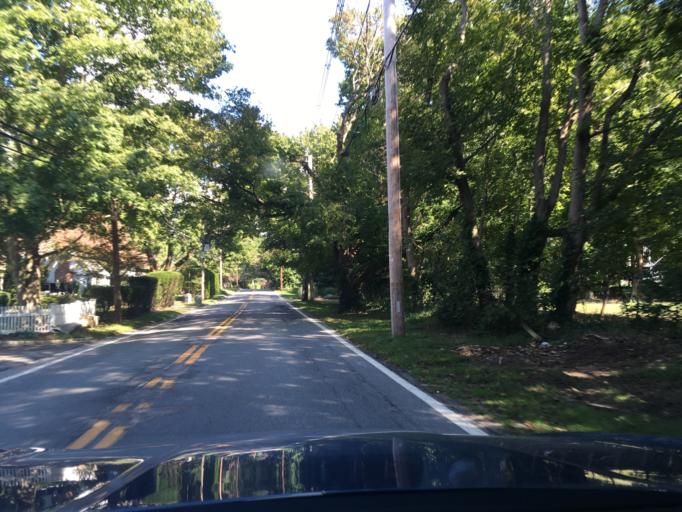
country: US
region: Rhode Island
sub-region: Bristol County
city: Barrington
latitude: 41.7291
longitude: -71.3212
